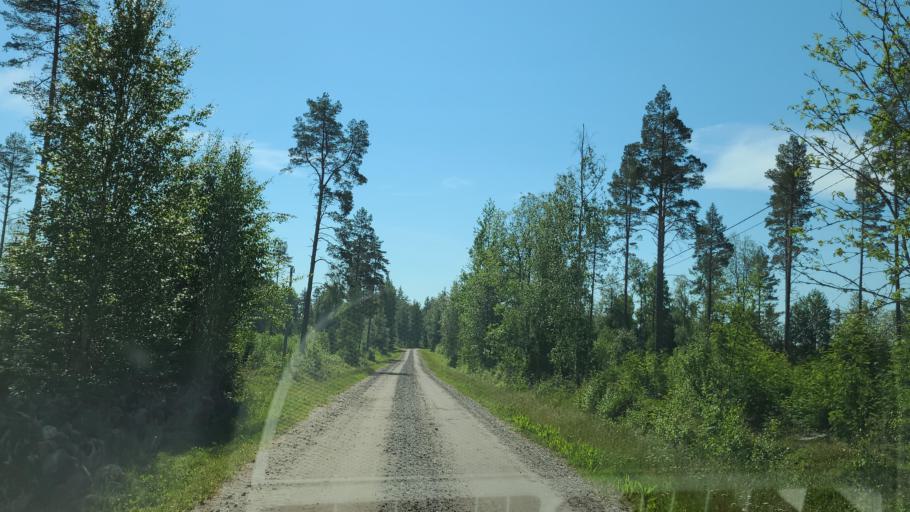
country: SE
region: Vaesterbotten
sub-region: Robertsfors Kommun
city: Robertsfors
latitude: 64.0914
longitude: 20.8484
